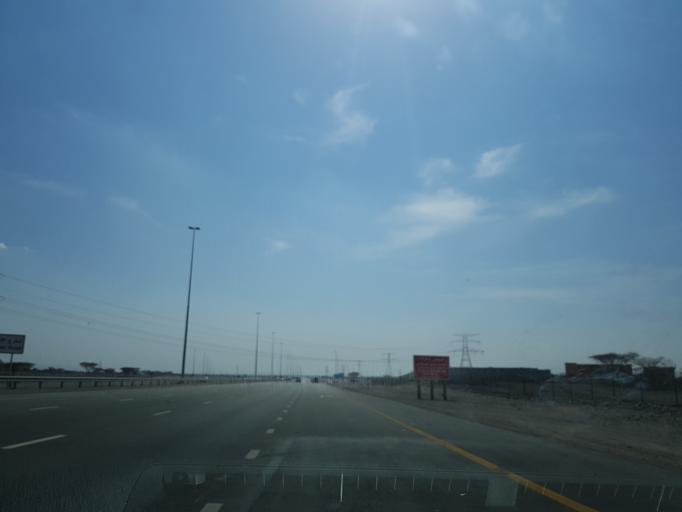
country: AE
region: Ra's al Khaymah
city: Ras al-Khaimah
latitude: 25.7691
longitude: 56.0257
